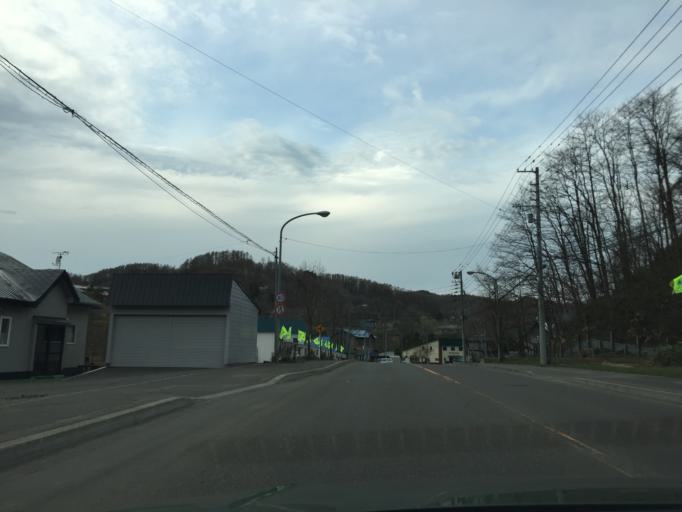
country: JP
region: Hokkaido
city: Utashinai
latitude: 43.5152
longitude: 142.0269
